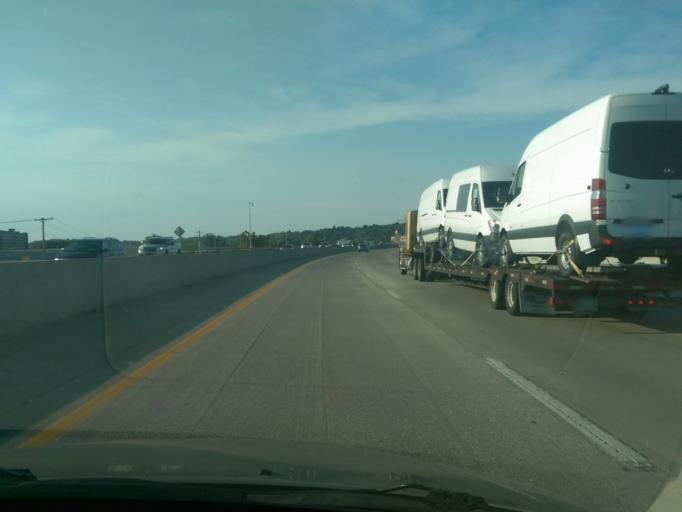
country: US
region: Missouri
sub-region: Clay County
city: North Kansas City
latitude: 39.1355
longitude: -94.5679
